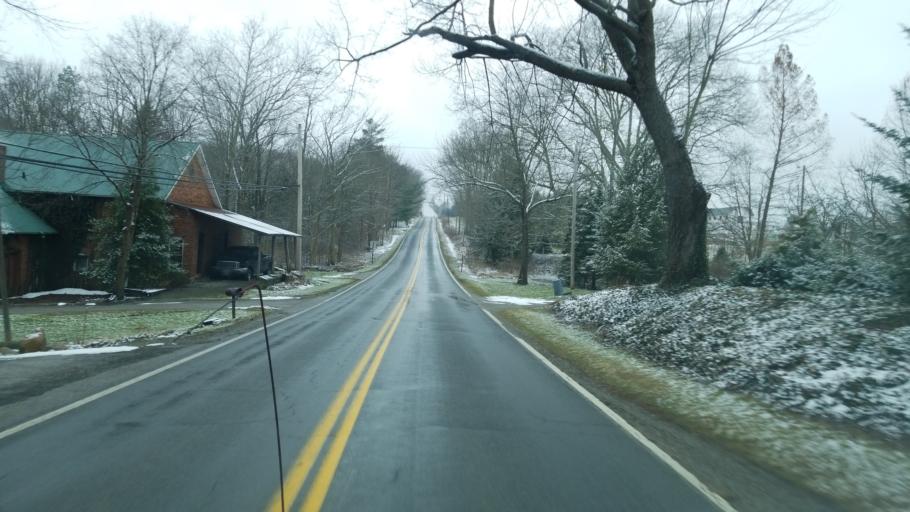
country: US
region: Ohio
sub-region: Portage County
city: Mantua
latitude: 41.2841
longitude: -81.2532
